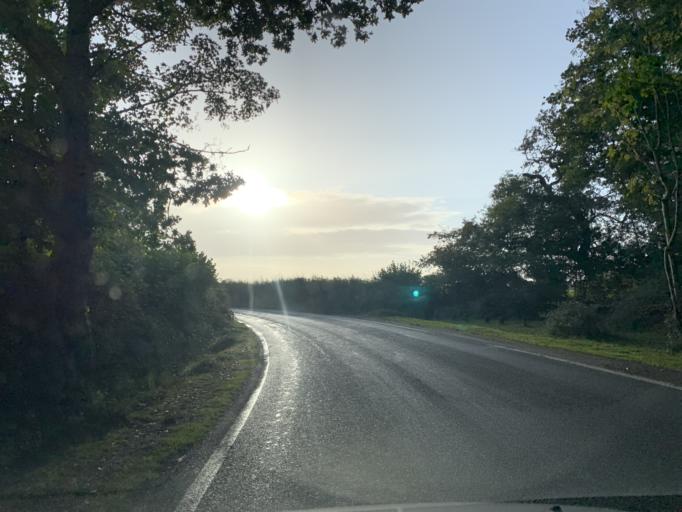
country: GB
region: England
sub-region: Hampshire
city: West Wellow
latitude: 50.9487
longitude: -1.6269
